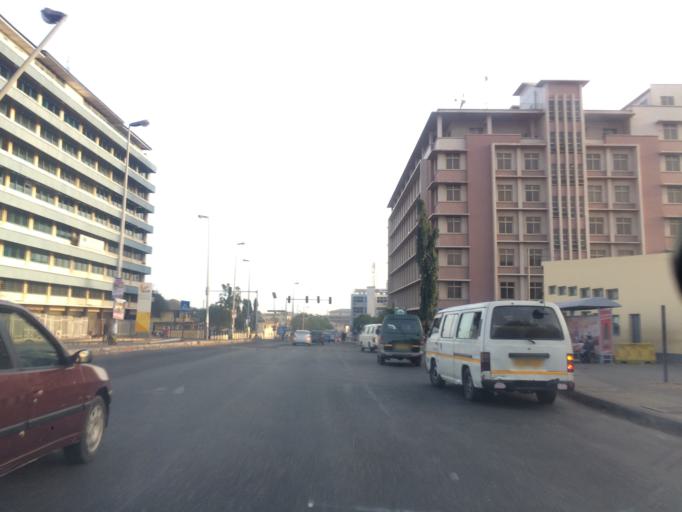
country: GH
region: Greater Accra
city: Accra
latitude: 5.5527
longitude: -0.2110
